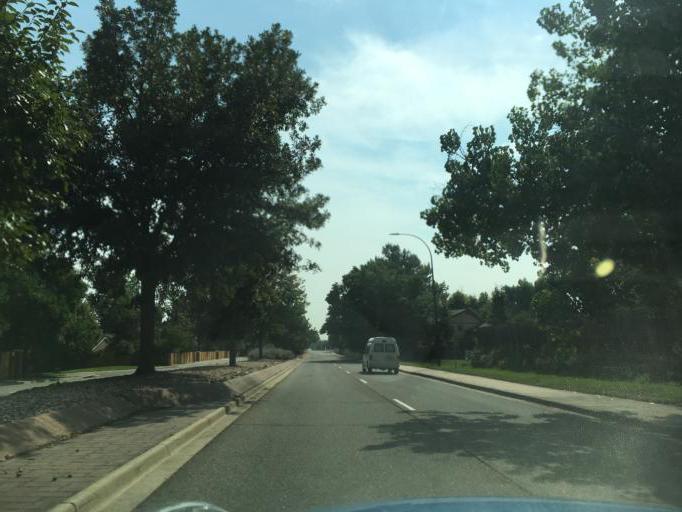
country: US
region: Colorado
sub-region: Jefferson County
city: Arvada
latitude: 39.8418
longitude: -105.0957
